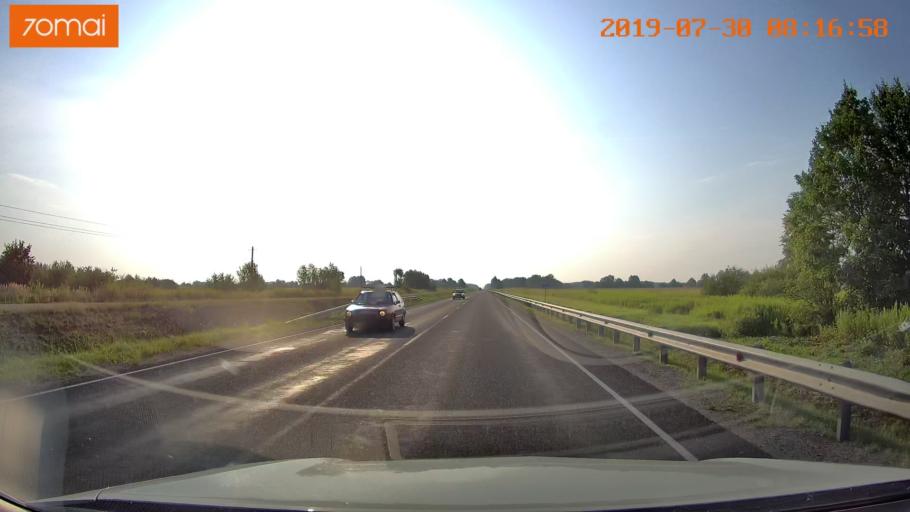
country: RU
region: Kaliningrad
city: Zheleznodorozhnyy
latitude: 54.6382
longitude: 21.4249
